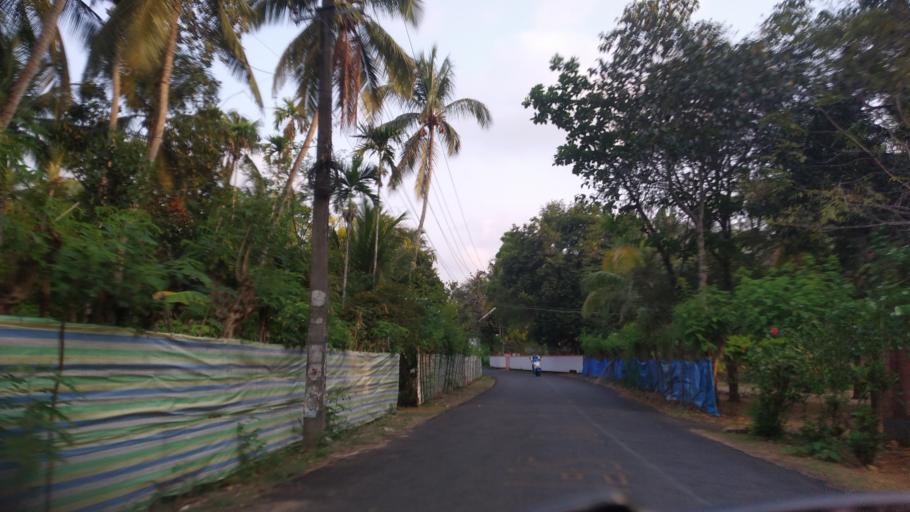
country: IN
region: Kerala
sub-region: Thrissur District
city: Thanniyam
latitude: 10.3565
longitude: 76.1113
